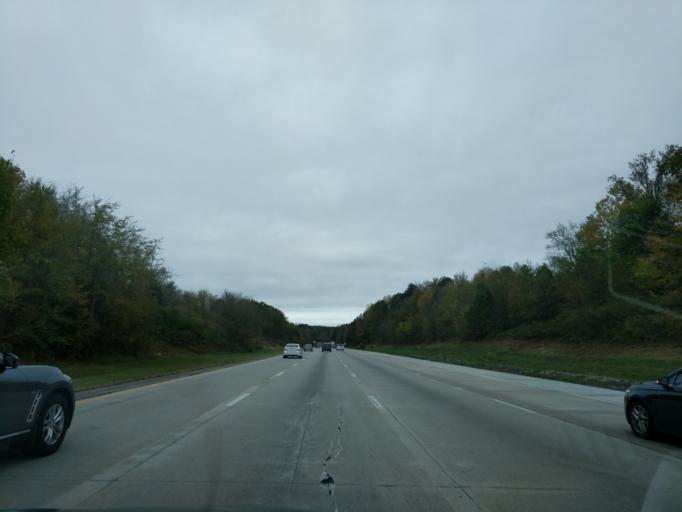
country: US
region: North Carolina
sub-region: Randolph County
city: Archdale
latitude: 35.9344
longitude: -79.9146
